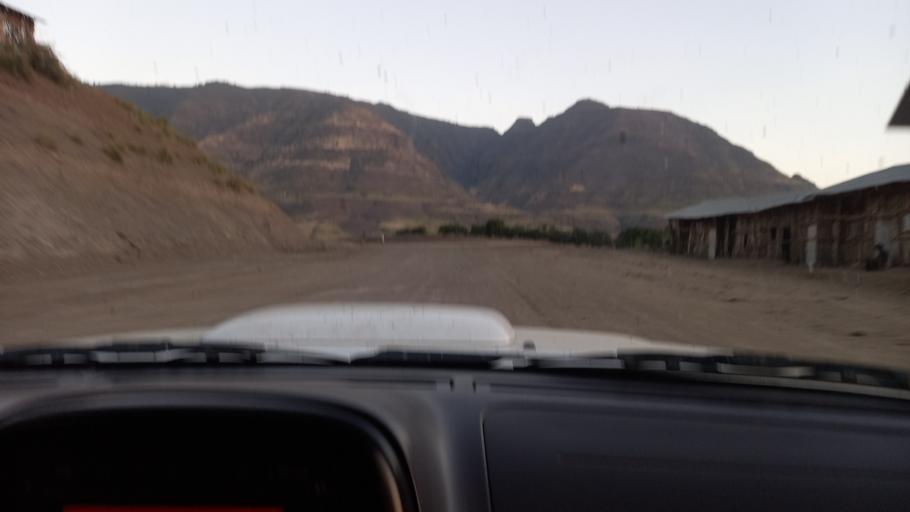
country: ET
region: Amhara
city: Debark'
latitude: 13.0368
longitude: 38.0411
